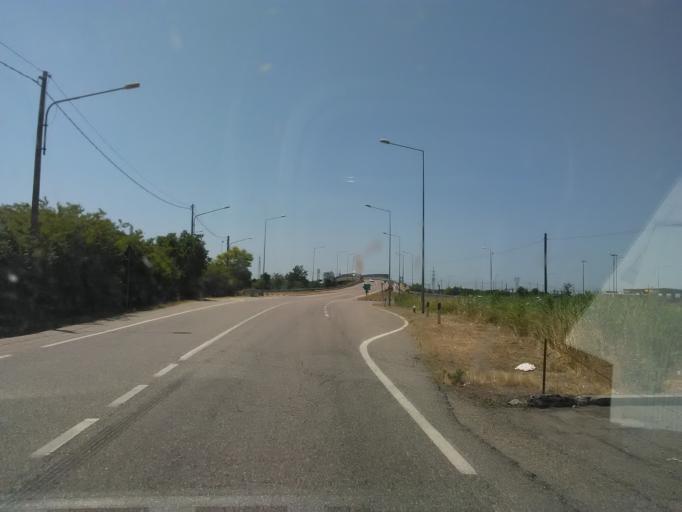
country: IT
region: Piedmont
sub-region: Provincia di Vercelli
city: Greggio
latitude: 45.4654
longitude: 8.3865
